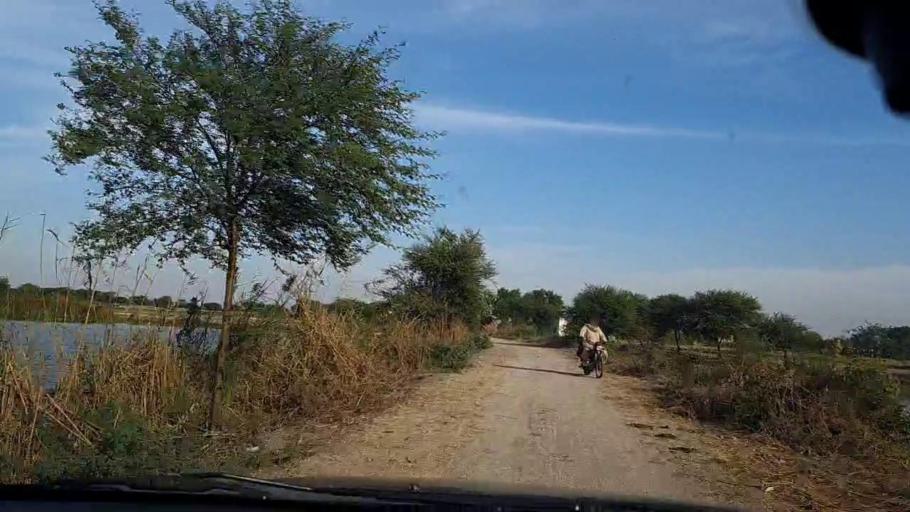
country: PK
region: Sindh
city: Mirpur Batoro
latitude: 24.6520
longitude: 68.2942
